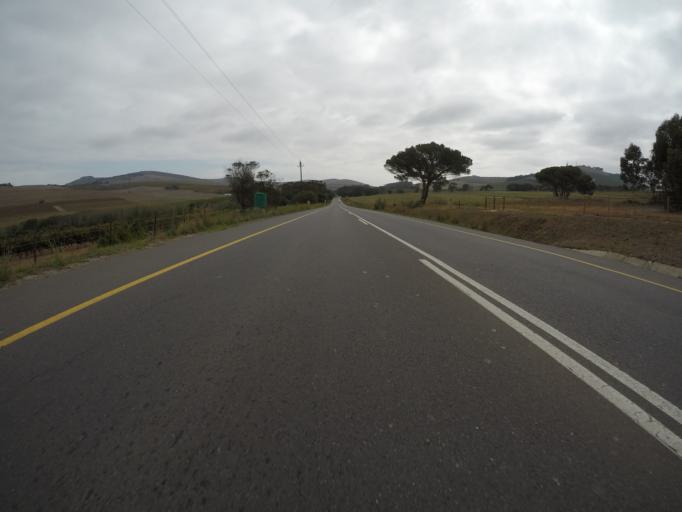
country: ZA
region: Western Cape
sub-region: City of Cape Town
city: Kraaifontein
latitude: -33.8426
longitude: 18.6197
